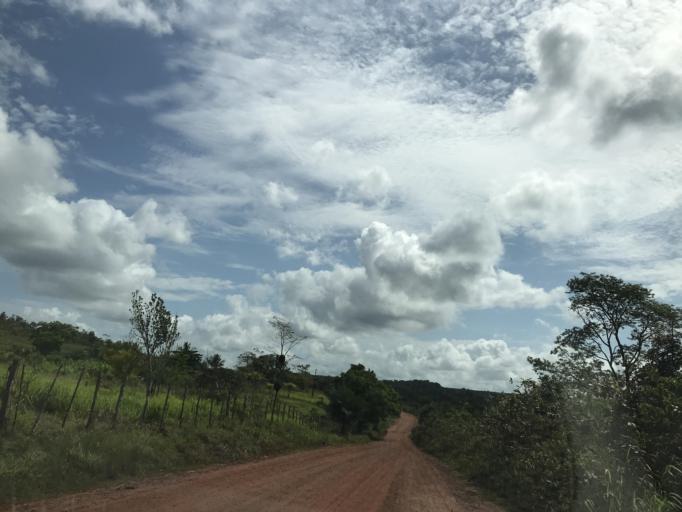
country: BR
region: Bahia
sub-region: Entre Rios
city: Entre Rios
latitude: -12.1669
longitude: -38.0860
